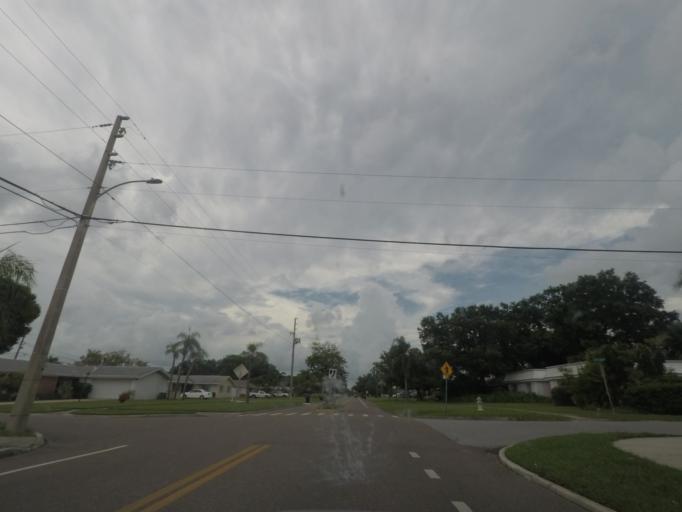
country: US
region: Florida
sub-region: Pinellas County
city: Kenneth City
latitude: 27.7990
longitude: -82.7273
